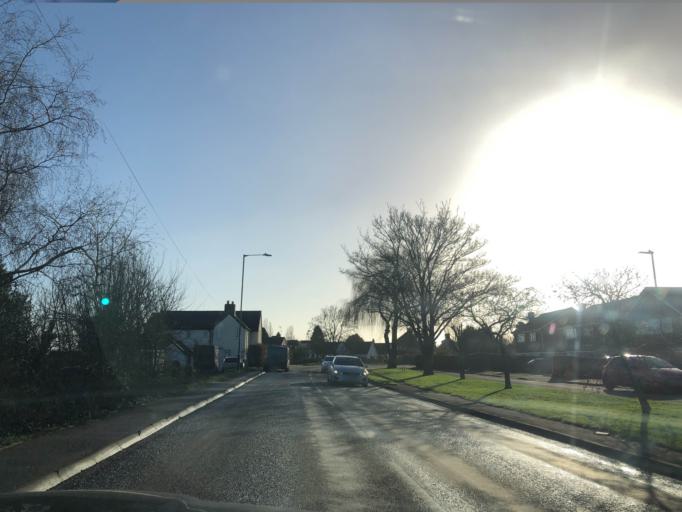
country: GB
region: England
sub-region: Warwickshire
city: Wellesbourne Mountford
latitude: 52.1944
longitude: -1.5880
